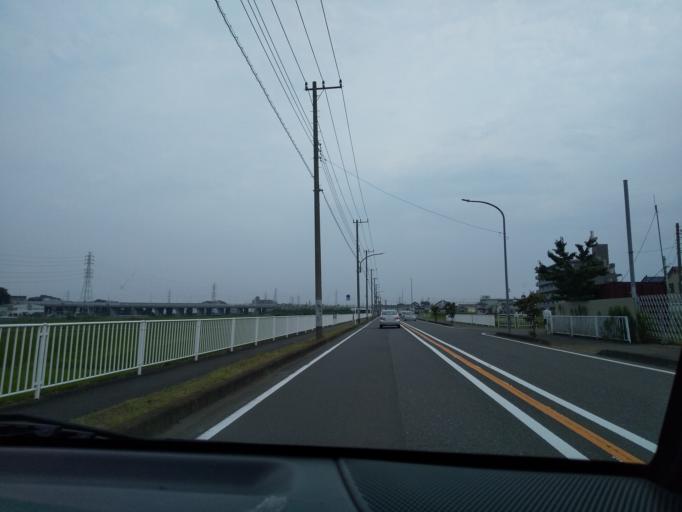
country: JP
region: Kanagawa
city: Atsugi
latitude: 35.4299
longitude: 139.3904
